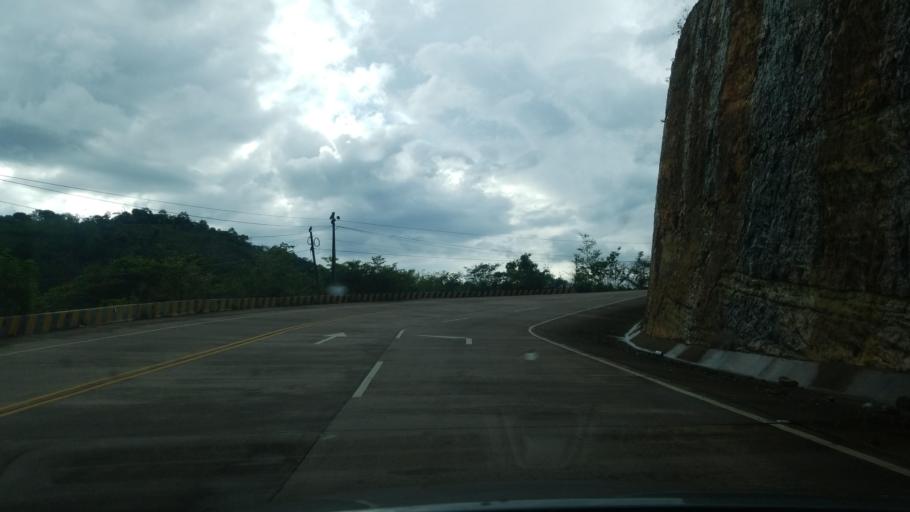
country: HN
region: Copan
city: Copan
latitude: 14.8371
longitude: -89.1860
